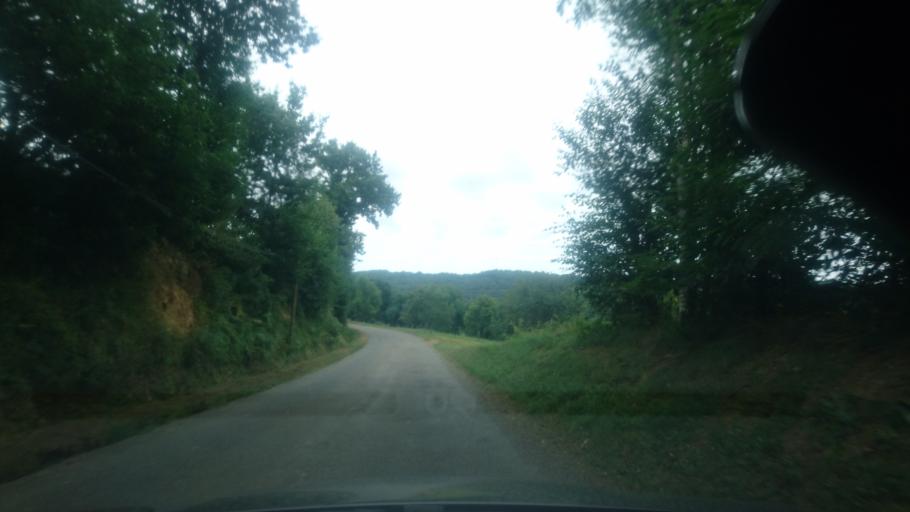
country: FR
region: Midi-Pyrenees
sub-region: Departement des Hautes-Pyrenees
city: Odos
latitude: 43.1427
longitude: 0.0422
